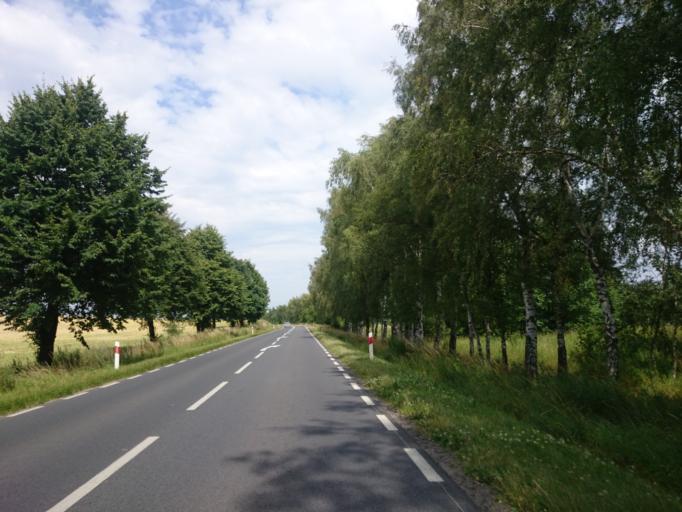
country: PL
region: West Pomeranian Voivodeship
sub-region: Powiat gryfinski
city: Chojna
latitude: 52.9435
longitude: 14.3946
